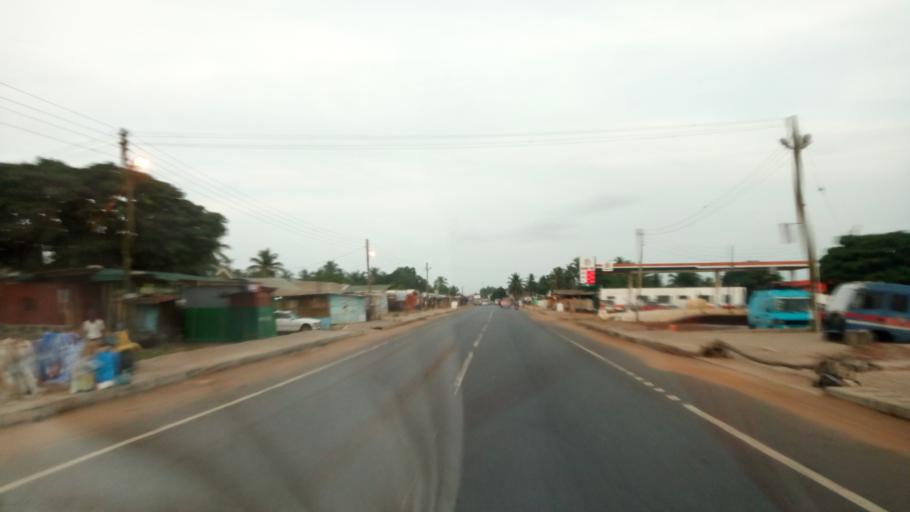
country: TG
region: Maritime
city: Lome
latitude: 6.1089
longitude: 1.1565
